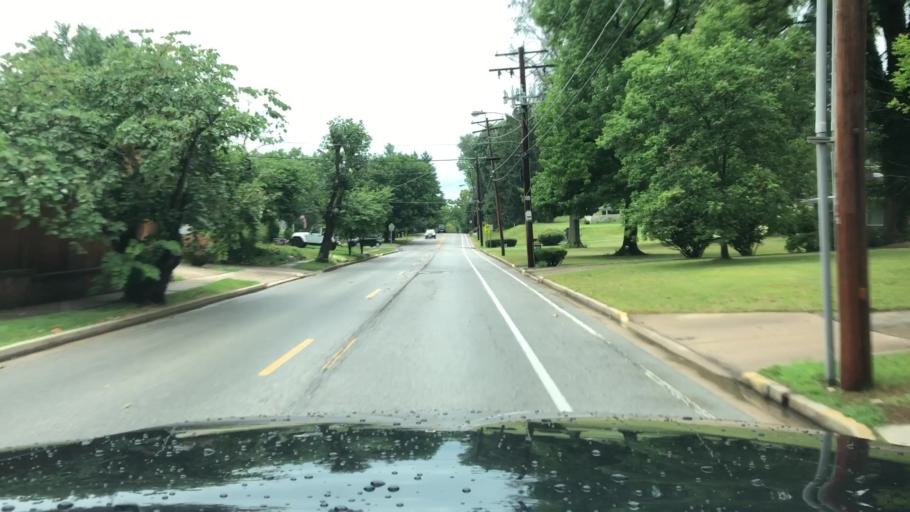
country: US
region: Missouri
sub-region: Saint Charles County
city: Saint Charles
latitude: 38.7893
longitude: -90.4965
